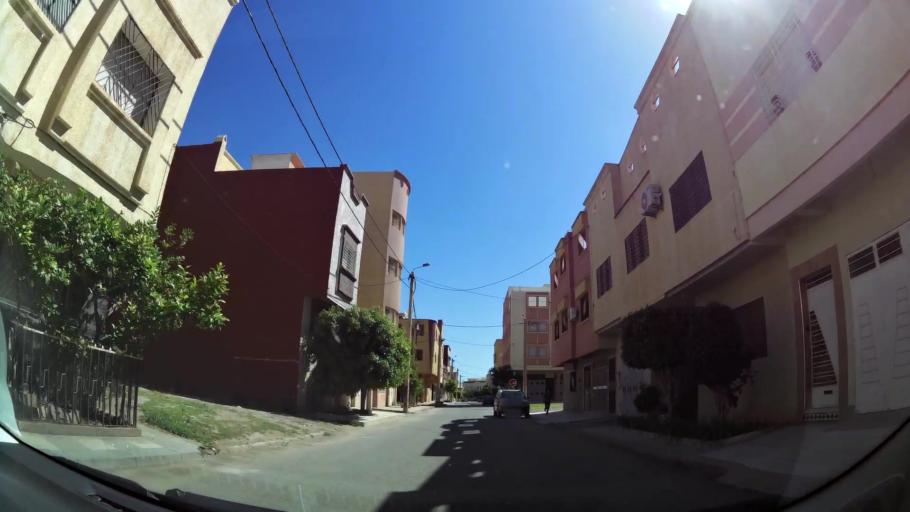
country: MA
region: Oriental
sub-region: Oujda-Angad
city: Oujda
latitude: 34.6570
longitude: -1.8900
